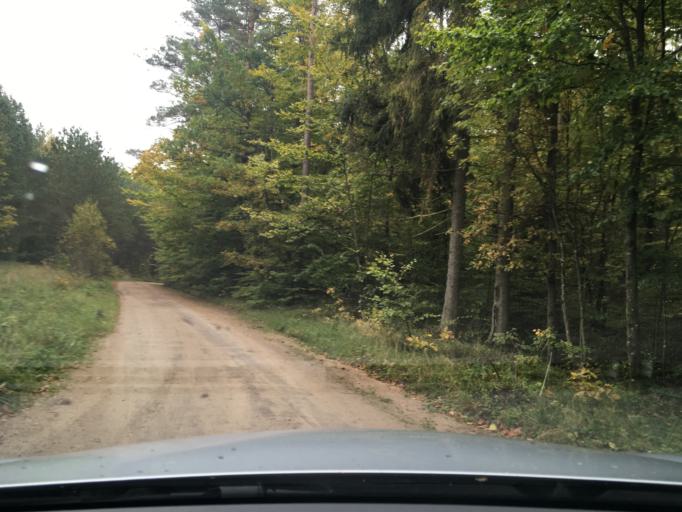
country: PL
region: Pomeranian Voivodeship
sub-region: Powiat koscierski
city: Koscierzyna
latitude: 54.0987
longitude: 17.9677
